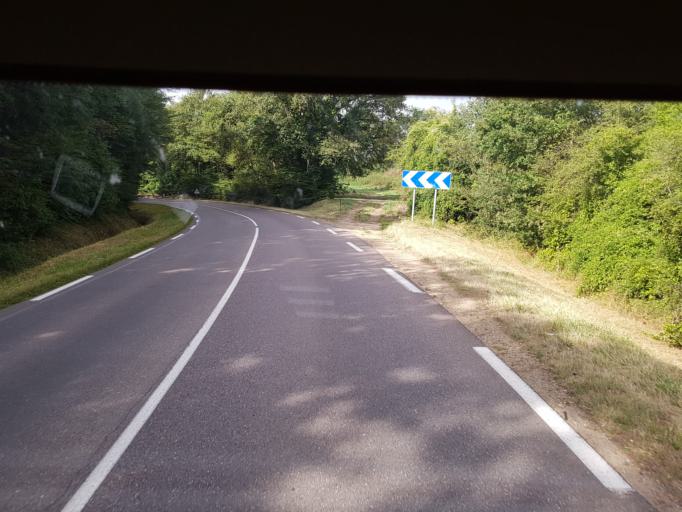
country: FR
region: Lorraine
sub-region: Departement de la Moselle
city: Koenigsmacker
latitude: 49.4197
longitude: 6.3191
